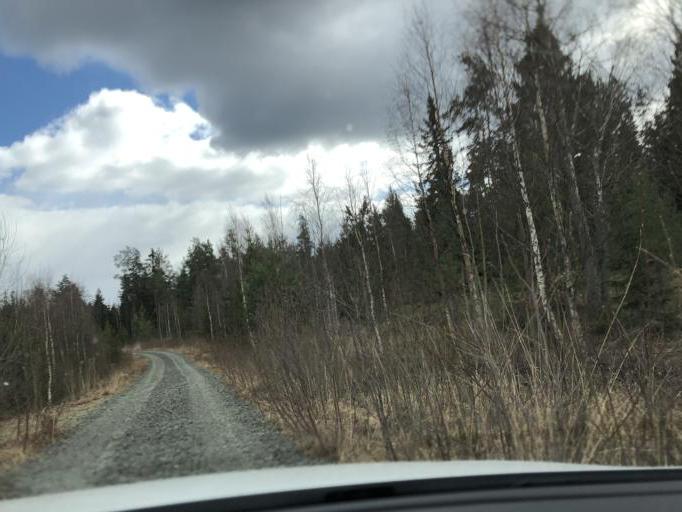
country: SE
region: Uppsala
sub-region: Heby Kommun
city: OEstervala
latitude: 60.3357
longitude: 17.1671
